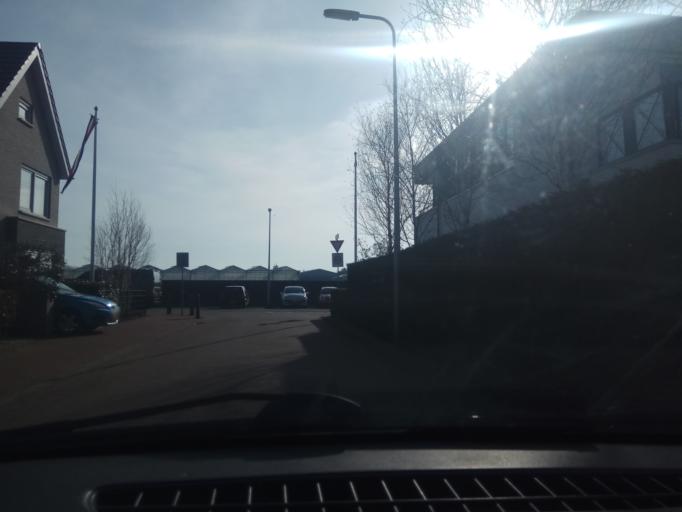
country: NL
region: South Holland
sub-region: Gemeente Westland
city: Monster
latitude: 52.0101
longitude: 4.1847
